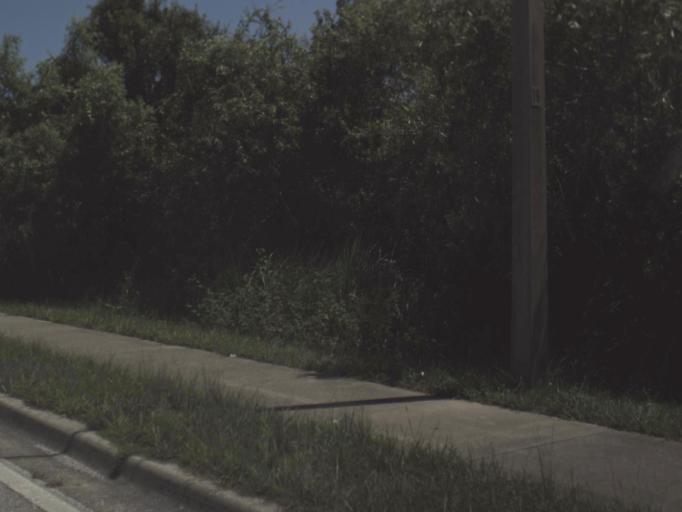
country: US
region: Florida
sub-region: Pinellas County
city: Pinellas Park
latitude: 27.8789
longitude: -82.7020
